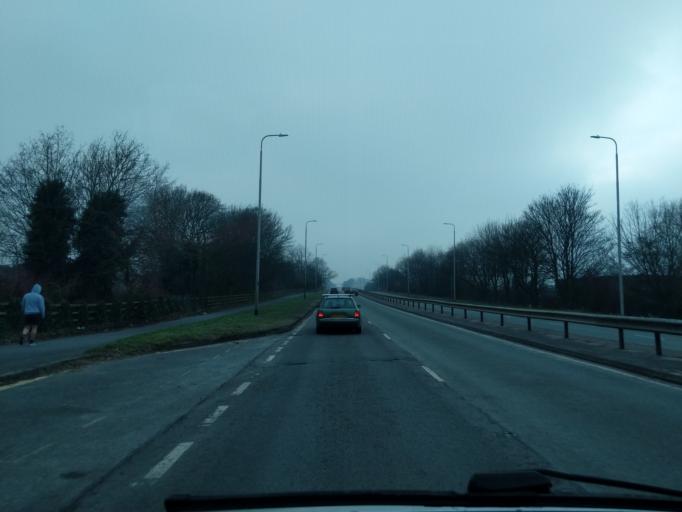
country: GB
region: England
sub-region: St. Helens
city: St Helens
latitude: 53.4718
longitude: -2.7326
